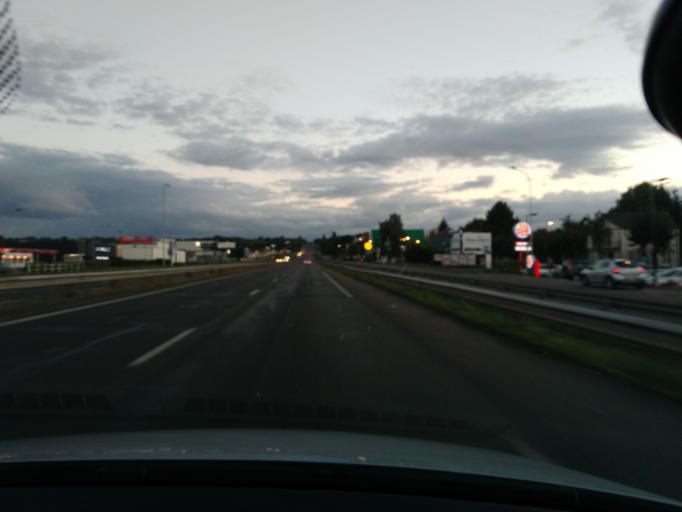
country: FR
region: Ile-de-France
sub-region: Departement de Seine-et-Marne
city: Villenoy
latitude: 48.9408
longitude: 2.8794
